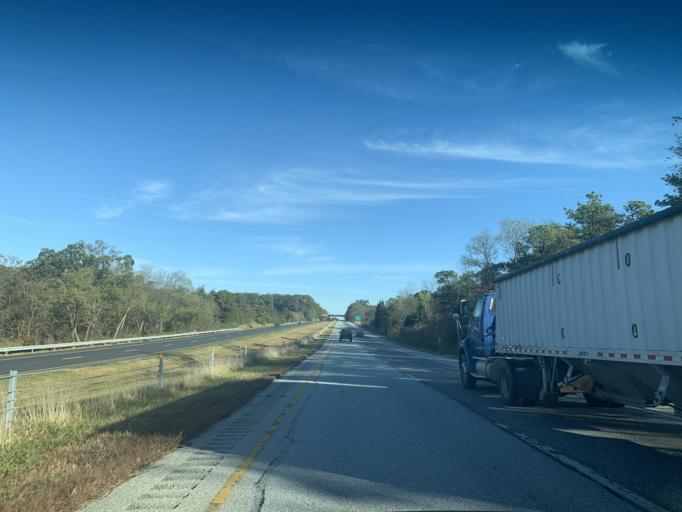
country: US
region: Maryland
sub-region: Cecil County
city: Rising Sun
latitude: 39.7360
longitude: -76.0244
